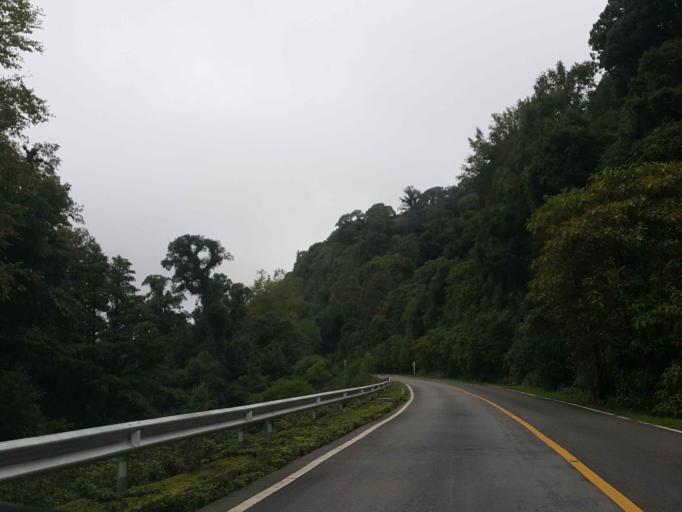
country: TH
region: Chiang Mai
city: Mae Chaem
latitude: 18.5626
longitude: 98.4840
